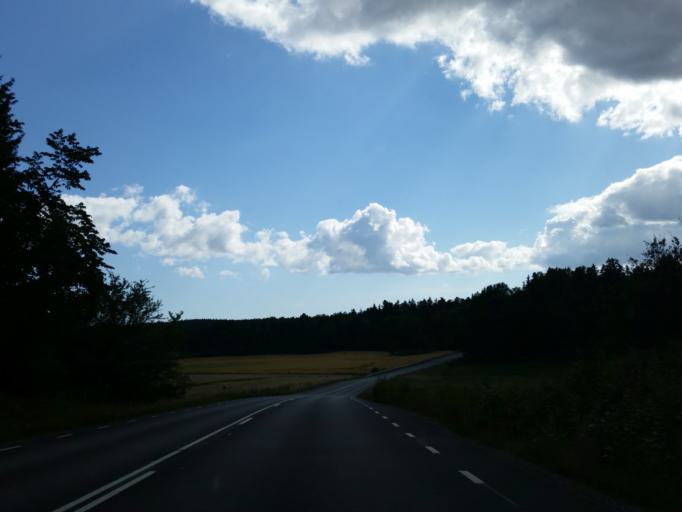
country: SE
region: Soedermanland
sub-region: Trosa Kommun
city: Vagnharad
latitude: 58.9596
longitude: 17.5600
